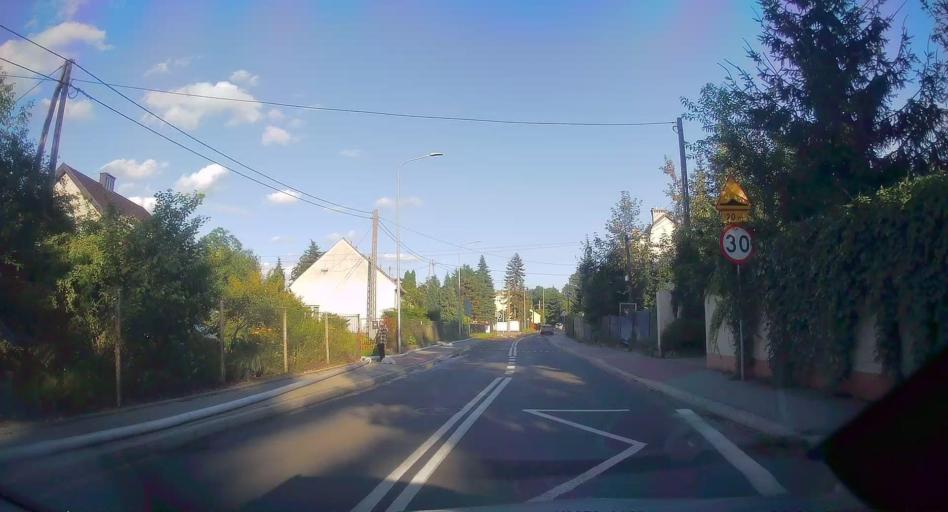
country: PL
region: Lesser Poland Voivodeship
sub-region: Powiat wielicki
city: Czarnochowice
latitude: 50.0193
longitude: 20.0239
